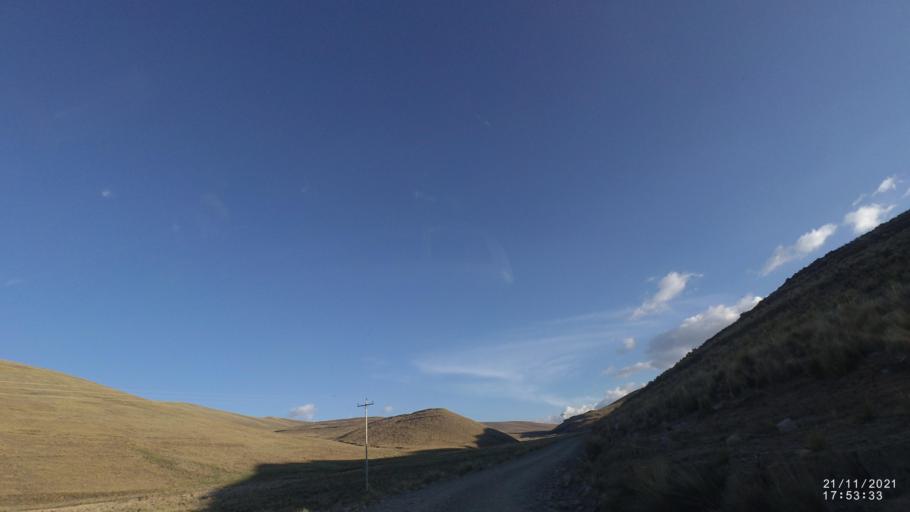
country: BO
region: Cochabamba
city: Cochabamba
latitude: -17.2141
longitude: -66.2387
